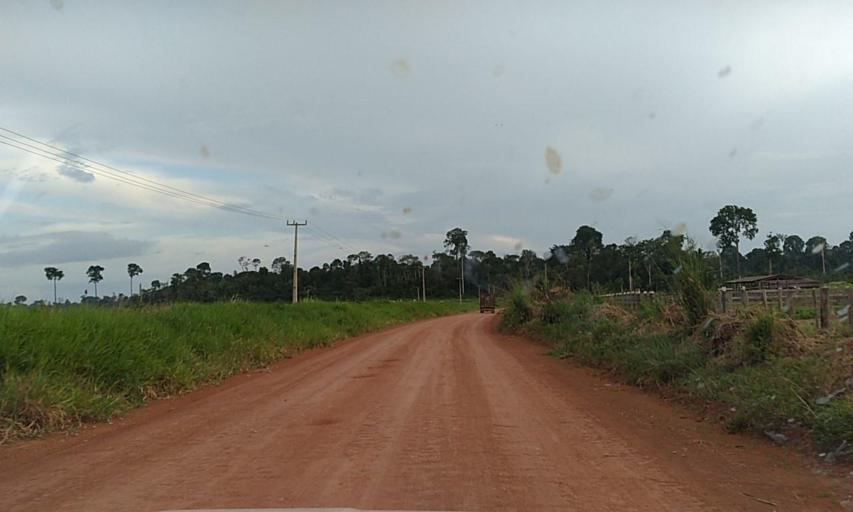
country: BR
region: Para
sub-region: Senador Jose Porfirio
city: Senador Jose Porfirio
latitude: -2.6989
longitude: -51.8210
